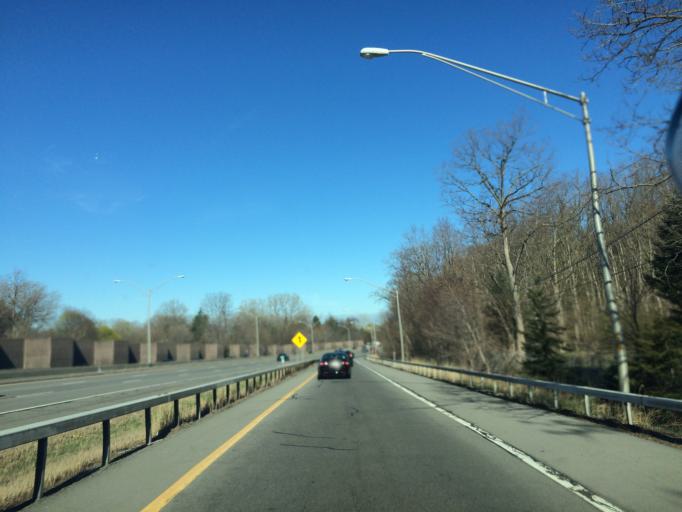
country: US
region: New York
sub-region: Monroe County
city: East Rochester
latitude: 43.1194
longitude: -77.5130
